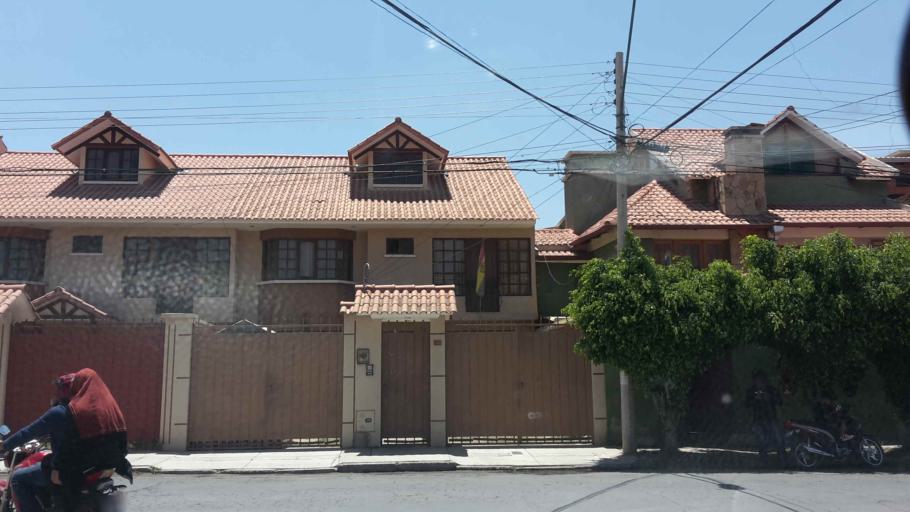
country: BO
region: Cochabamba
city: Cochabamba
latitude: -17.3773
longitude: -66.1927
